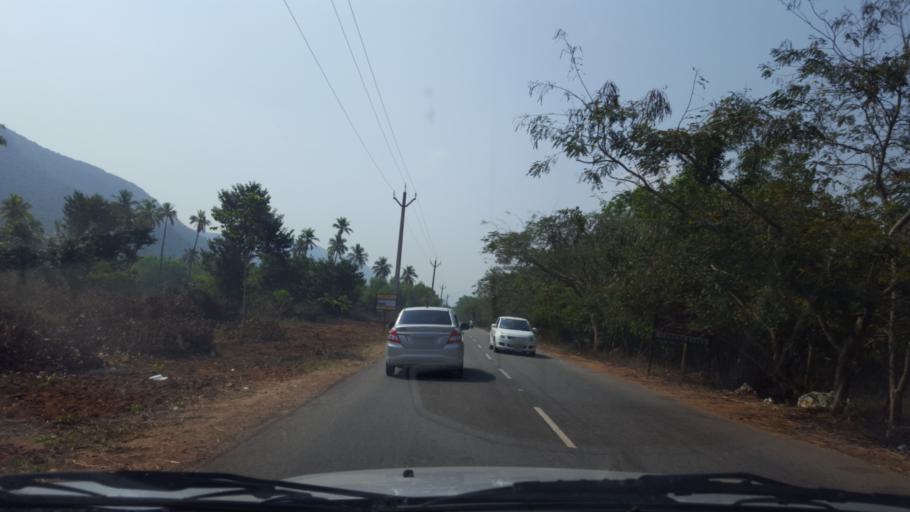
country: IN
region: Andhra Pradesh
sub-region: Vishakhapatnam
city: Vepagunta
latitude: 17.8421
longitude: 83.2657
